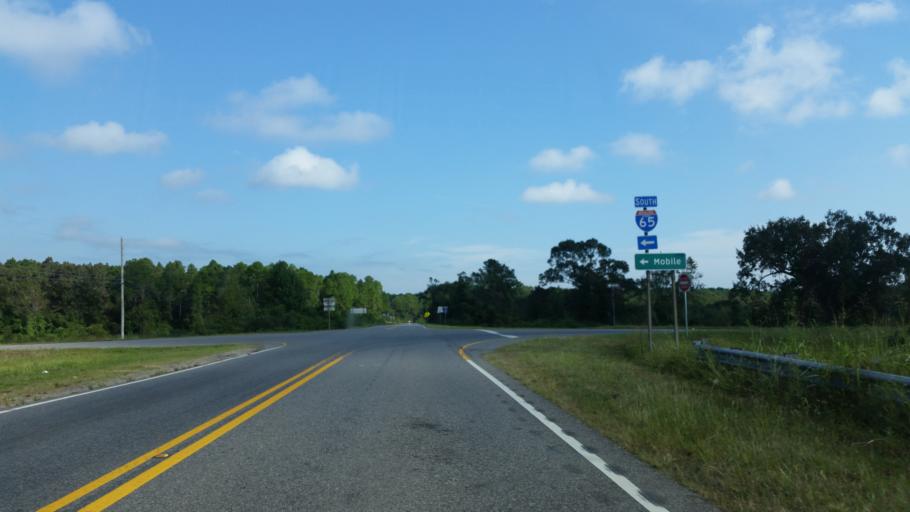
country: US
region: Alabama
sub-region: Baldwin County
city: Bay Minette
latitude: 30.9652
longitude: -87.7595
